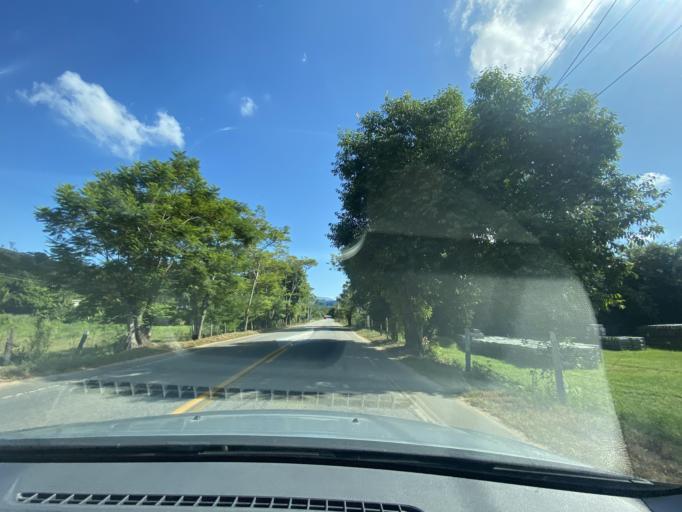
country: BR
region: Espirito Santo
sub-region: Jeronimo Monteiro
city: Jeronimo Monteiro
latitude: -20.7891
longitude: -41.4108
